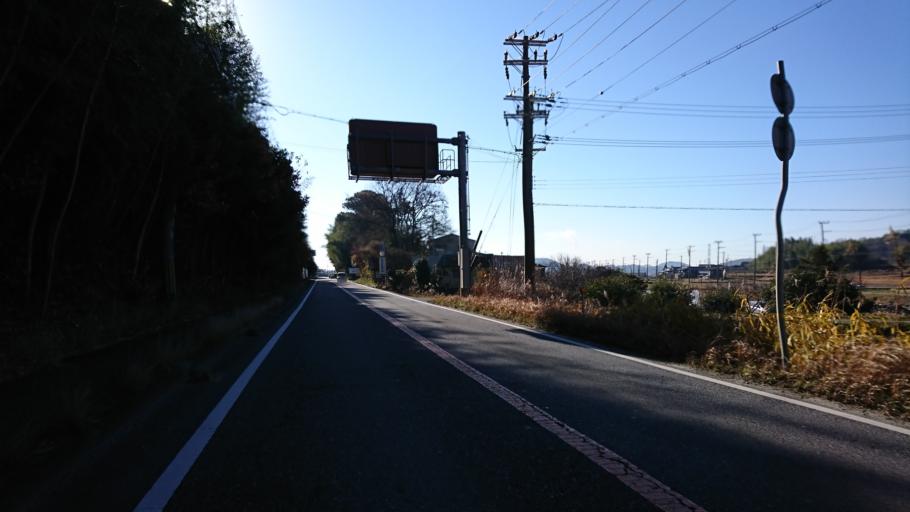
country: JP
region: Hyogo
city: Kakogawacho-honmachi
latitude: 34.8435
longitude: 134.8367
